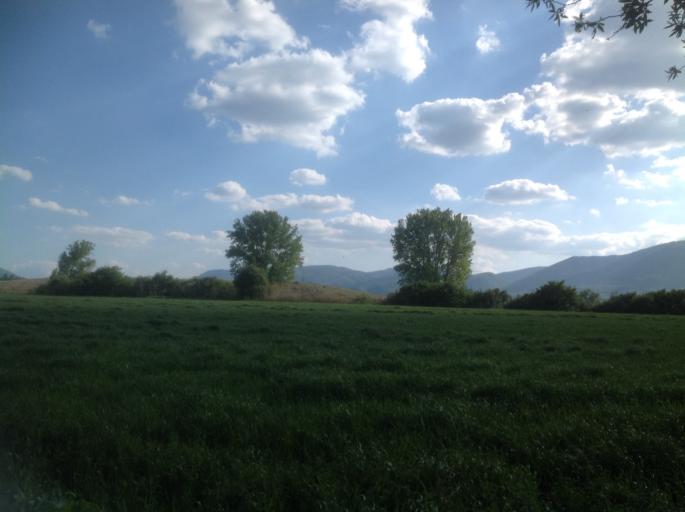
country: IT
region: Latium
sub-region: Provincia di Rieti
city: Colli sul Velino
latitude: 42.4693
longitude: 12.8060
